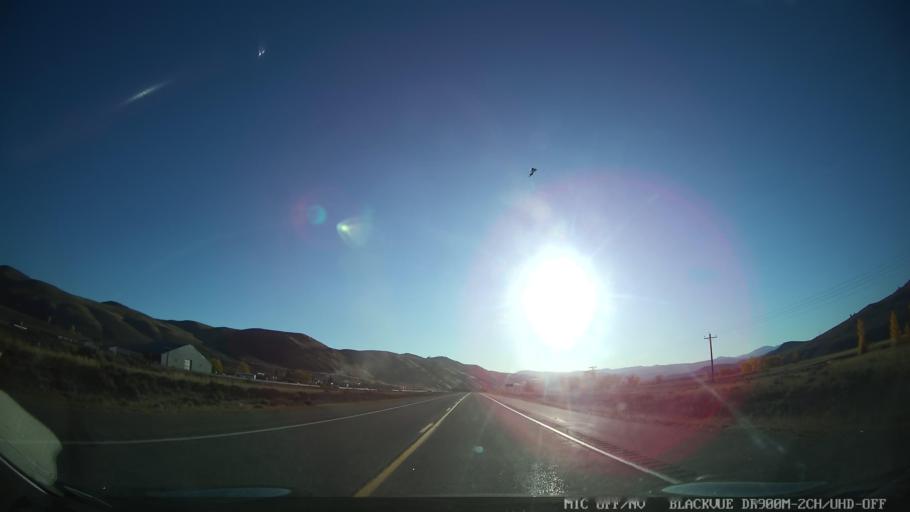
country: US
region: Colorado
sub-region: Grand County
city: Hot Sulphur Springs
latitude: 40.0671
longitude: -106.2108
